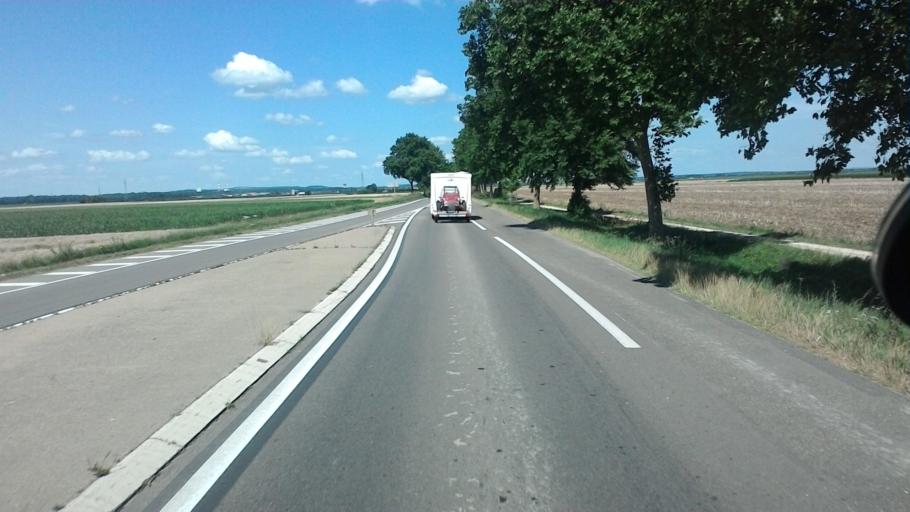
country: FR
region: Franche-Comte
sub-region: Departement du Jura
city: Tavaux
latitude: 47.0157
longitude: 5.3754
